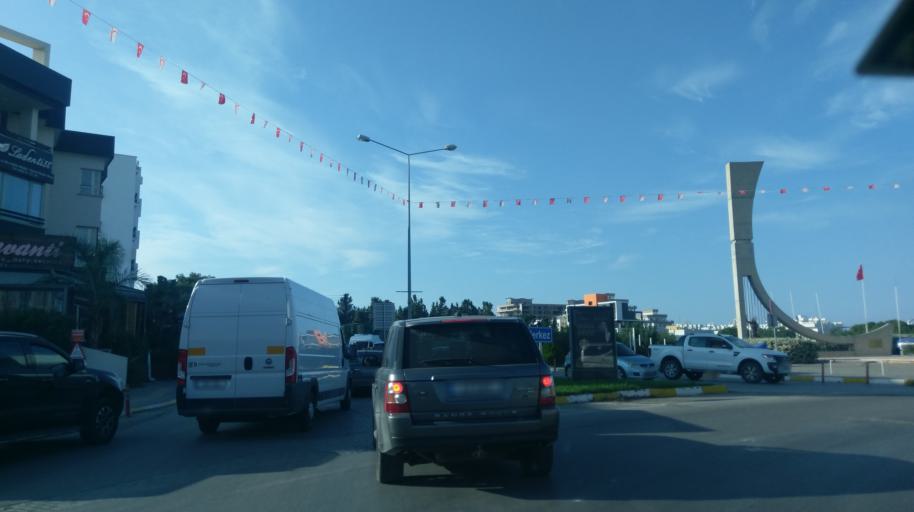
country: CY
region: Keryneia
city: Kyrenia
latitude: 35.3339
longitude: 33.3308
